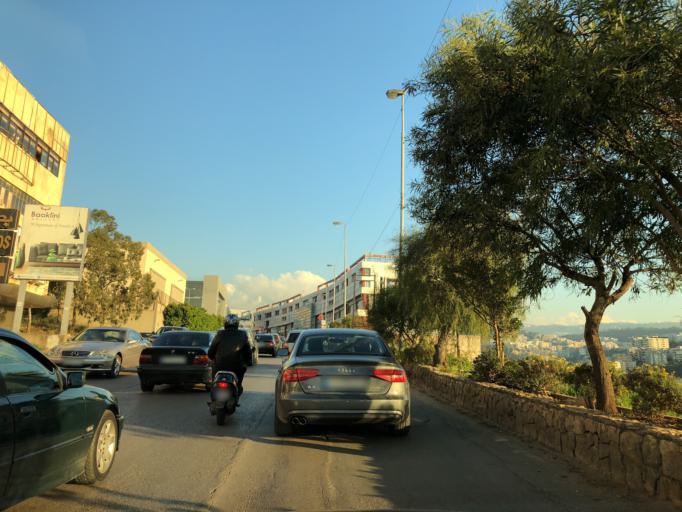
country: LB
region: Mont-Liban
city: Baabda
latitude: 33.8612
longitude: 35.5508
